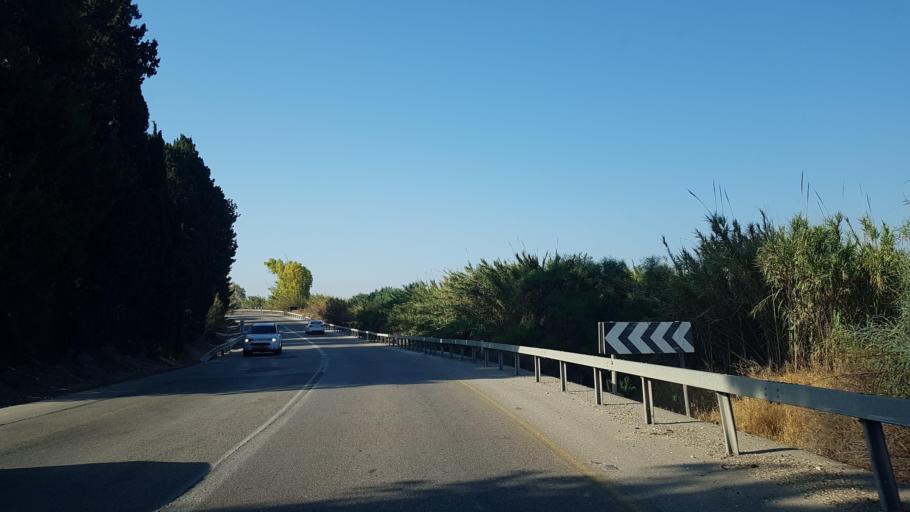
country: IL
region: Southern District
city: Ashdod
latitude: 31.7125
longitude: 34.6431
